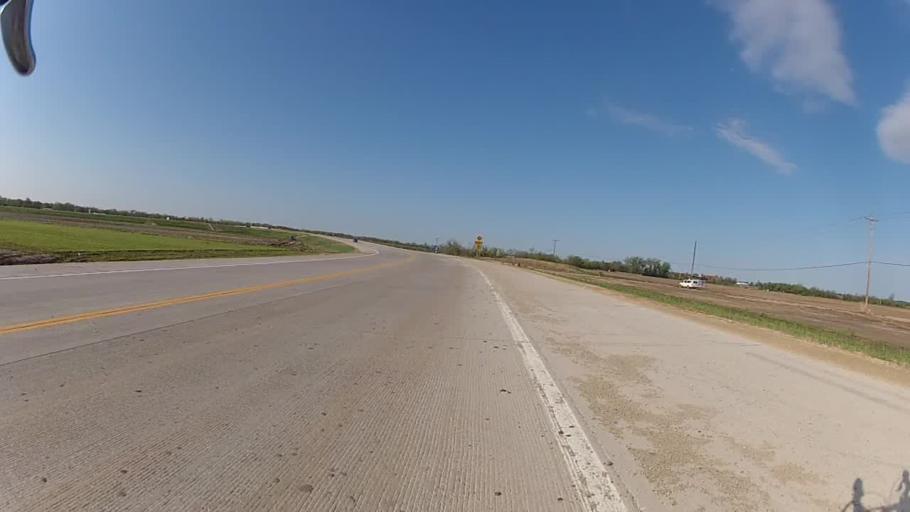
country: US
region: Kansas
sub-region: Riley County
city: Manhattan
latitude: 39.1599
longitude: -96.6440
